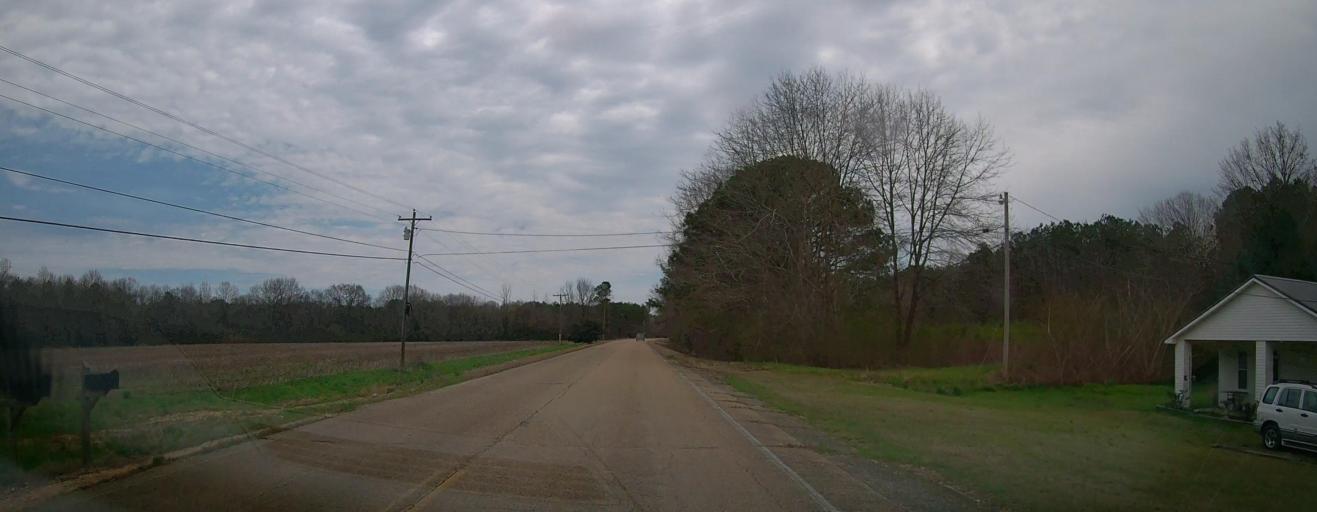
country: US
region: Mississippi
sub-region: Itawamba County
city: Fulton
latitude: 34.2305
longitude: -88.2428
